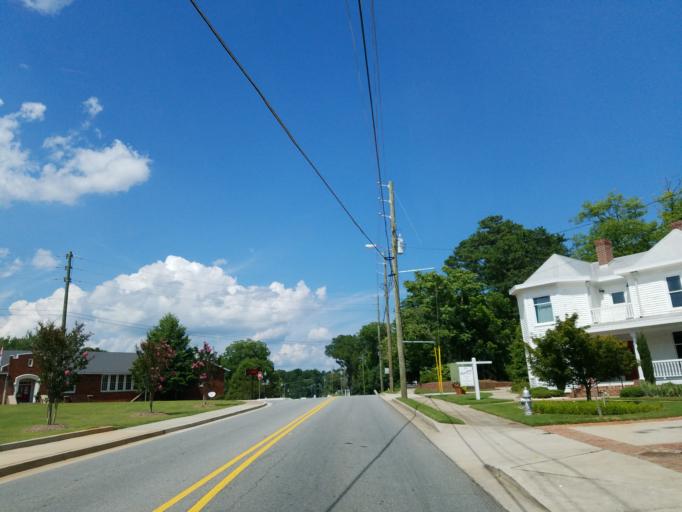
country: US
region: Georgia
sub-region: Forsyth County
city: Cumming
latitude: 34.2075
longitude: -84.1371
